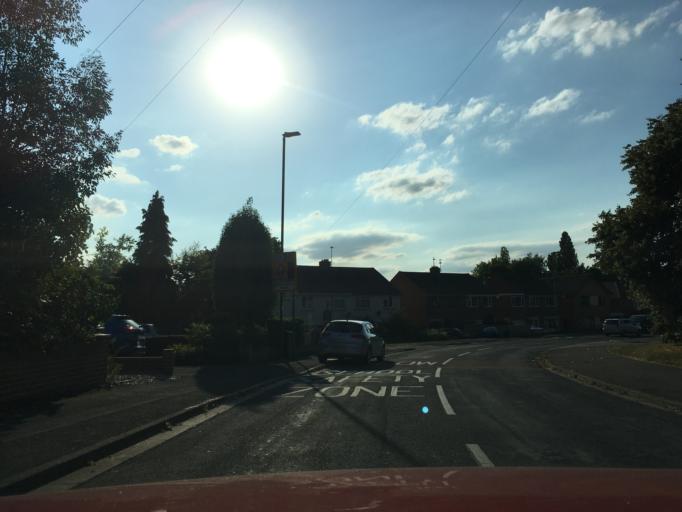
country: GB
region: England
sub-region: Gloucestershire
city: Churchdown
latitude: 51.8456
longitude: -2.1553
